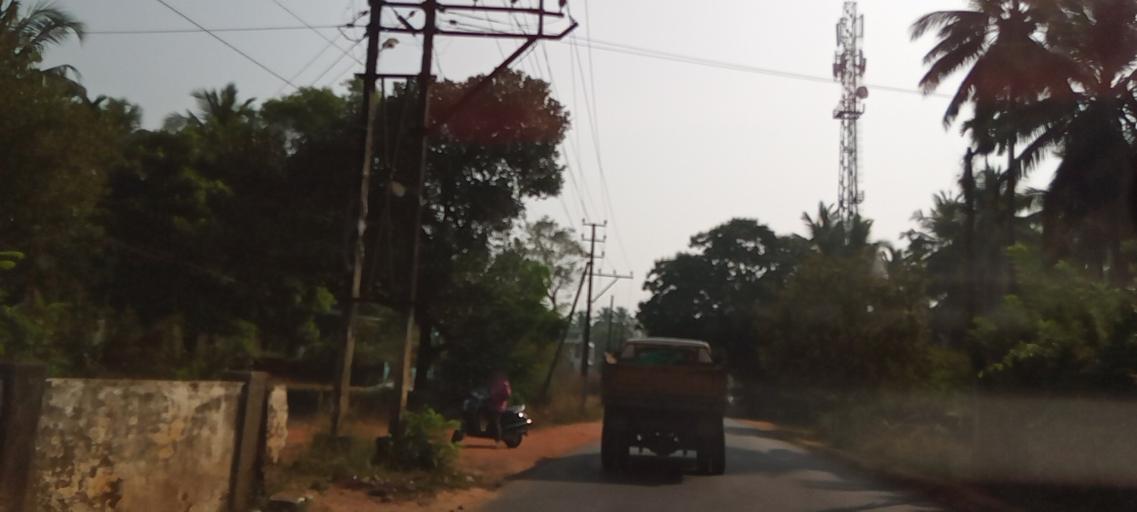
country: IN
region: Karnataka
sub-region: Udupi
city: Coondapoor
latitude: 13.5162
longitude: 74.7446
